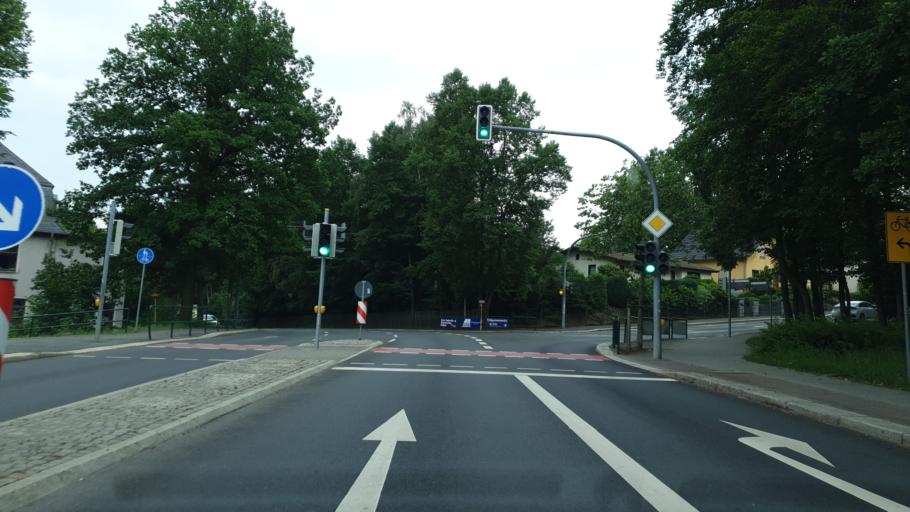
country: DE
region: Saxony
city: Auerbach
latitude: 50.5243
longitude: 12.3994
